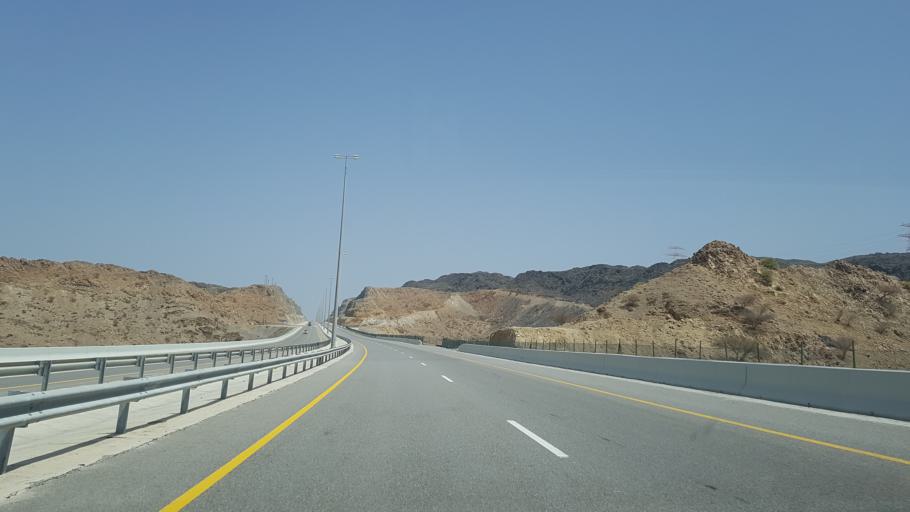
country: OM
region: Muhafazat Masqat
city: Muscat
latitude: 23.2154
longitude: 58.7958
